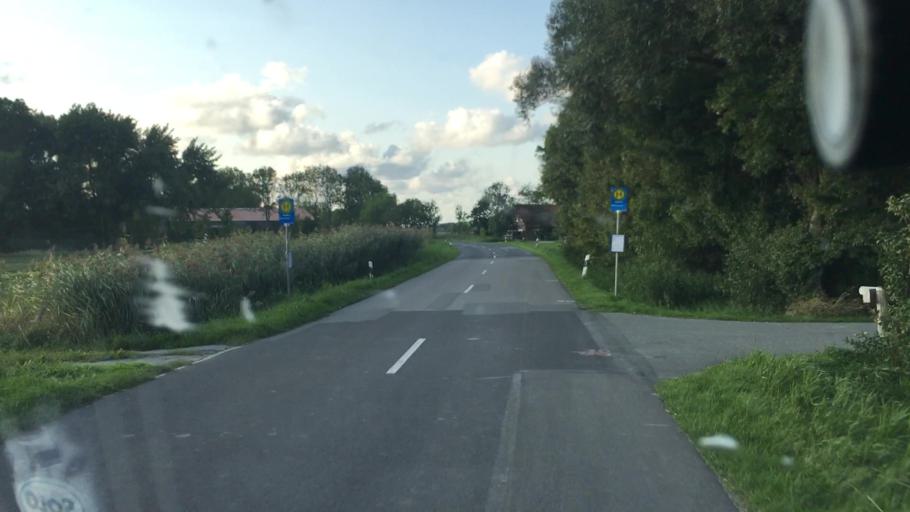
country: DE
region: Lower Saxony
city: Werdum
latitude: 53.6715
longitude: 7.7235
